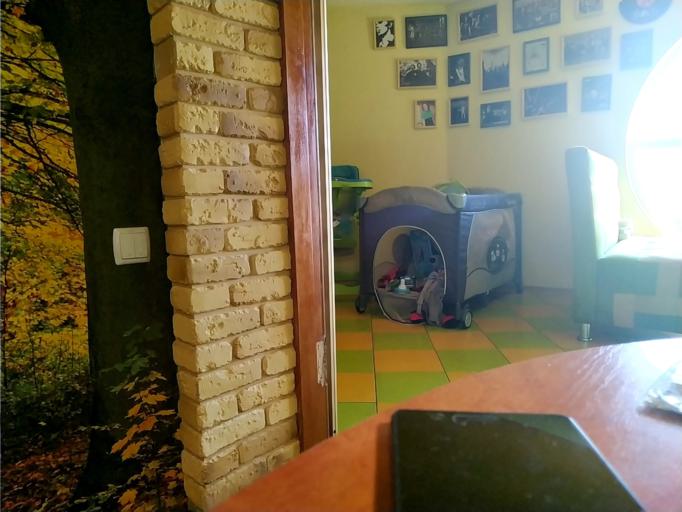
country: RU
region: Rjazan
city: Putyatino
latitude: 54.0870
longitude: 41.1554
